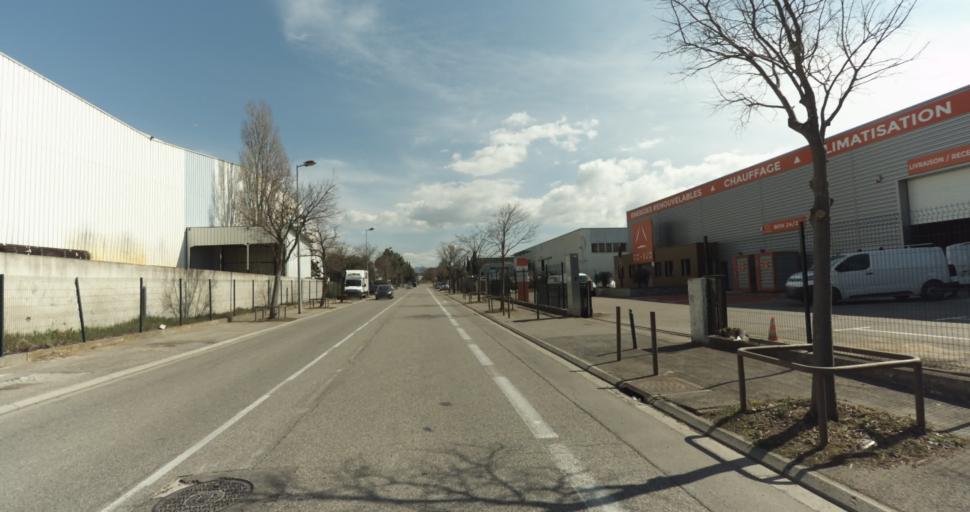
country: FR
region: Provence-Alpes-Cote d'Azur
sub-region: Departement des Bouches-du-Rhone
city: Cabries
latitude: 43.4827
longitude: 5.3775
